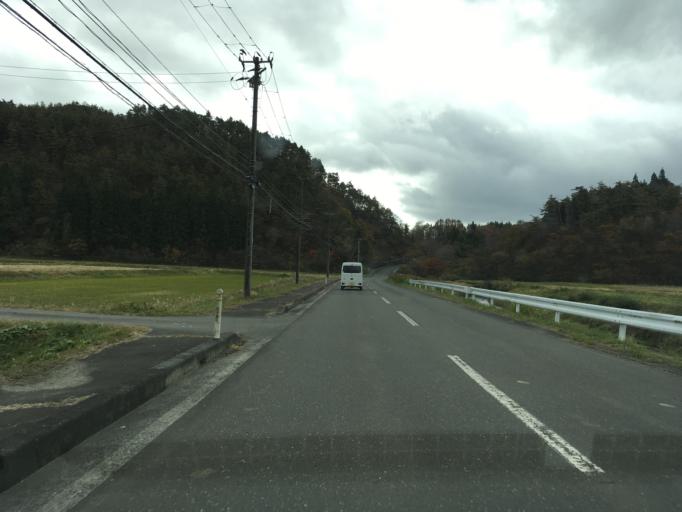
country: JP
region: Iwate
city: Mizusawa
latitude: 39.0690
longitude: 141.3548
